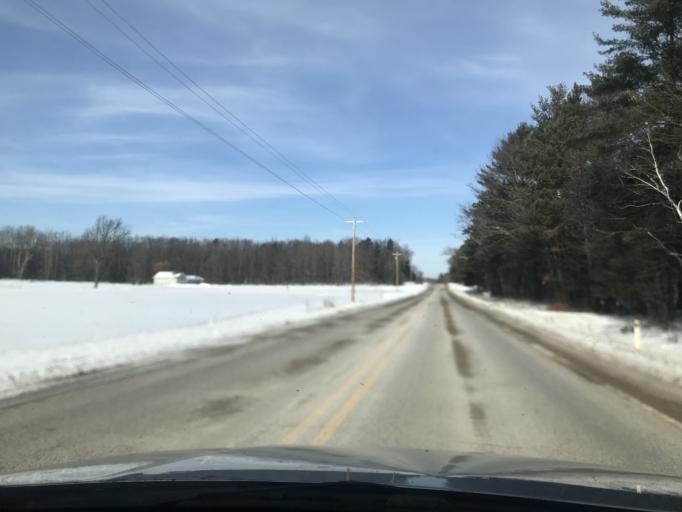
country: US
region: Wisconsin
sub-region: Oconto County
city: Oconto Falls
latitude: 45.1354
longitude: -88.1775
